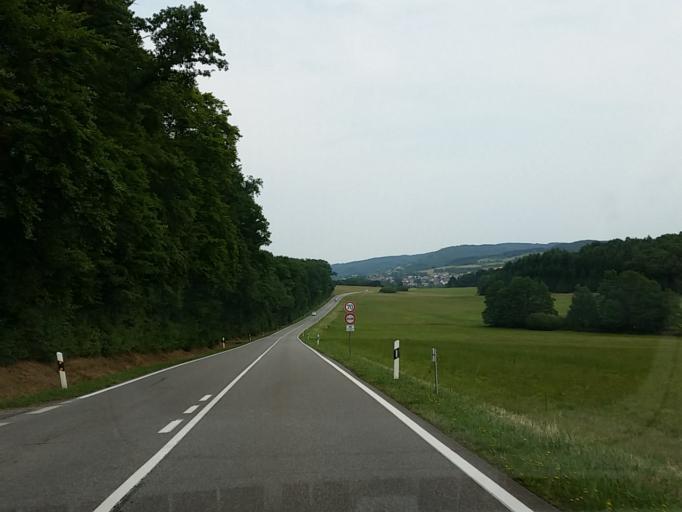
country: DE
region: Saarland
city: Wadern
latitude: 49.5512
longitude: 6.9099
